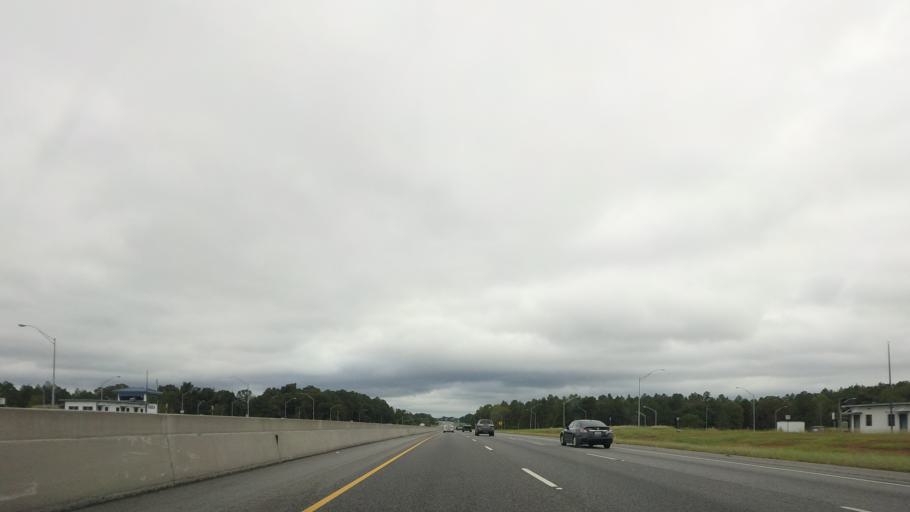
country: US
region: Georgia
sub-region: Lowndes County
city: Hahira
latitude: 30.9185
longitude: -83.3655
